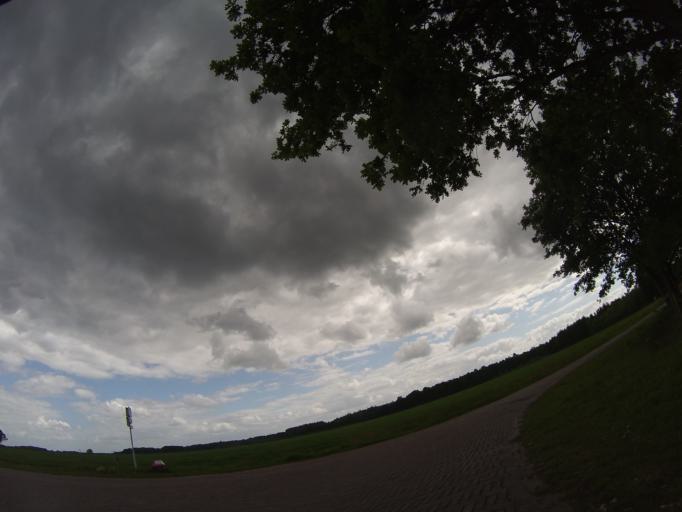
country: NL
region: Drenthe
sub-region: Gemeente Emmen
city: Emmen
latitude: 52.8390
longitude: 6.8741
